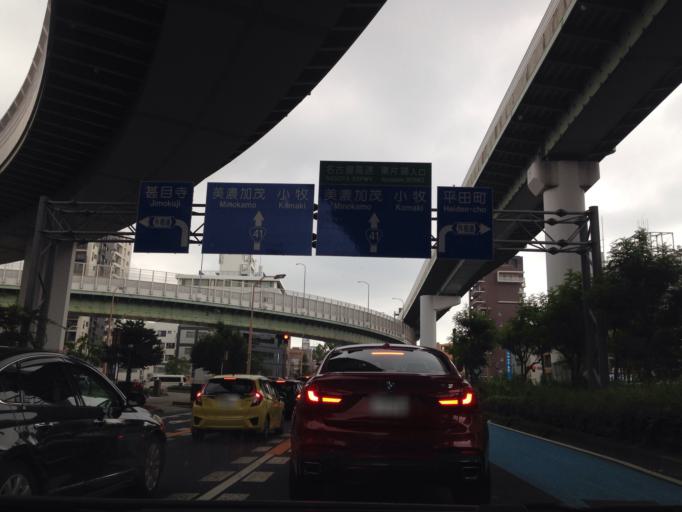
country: JP
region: Aichi
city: Nagoya-shi
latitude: 35.1779
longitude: 136.9139
